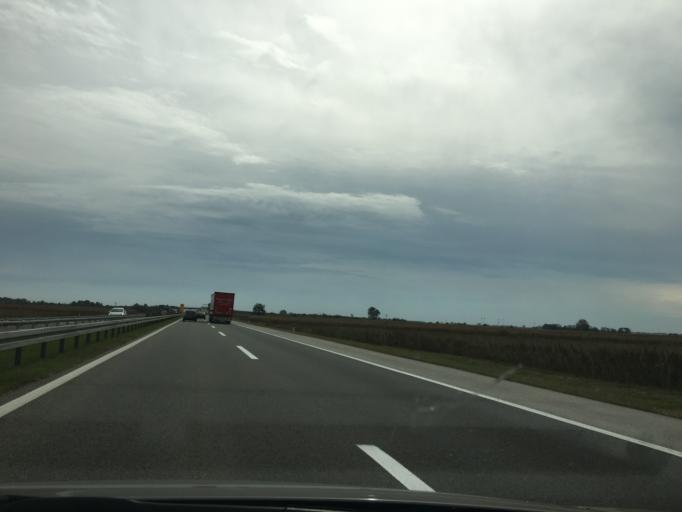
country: RS
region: Autonomna Pokrajina Vojvodina
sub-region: Sremski Okrug
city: Stara Pazova
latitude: 45.0167
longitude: 20.1955
